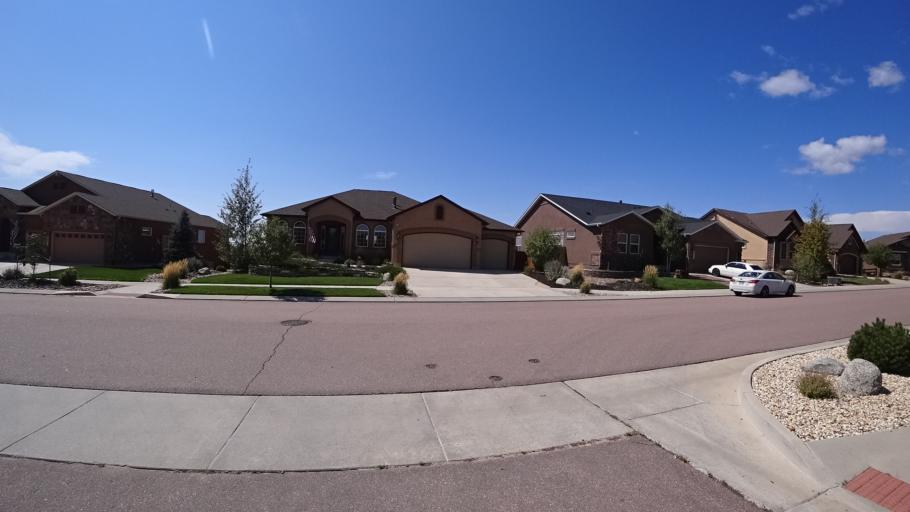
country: US
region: Colorado
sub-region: El Paso County
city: Cimarron Hills
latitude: 38.9286
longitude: -104.6907
